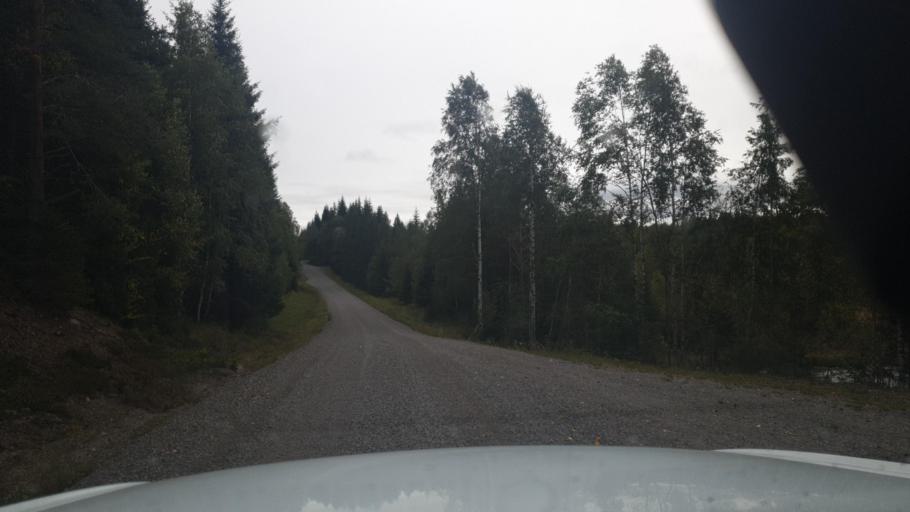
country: SE
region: Vaermland
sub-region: Eda Kommun
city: Charlottenberg
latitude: 60.1049
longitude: 12.6064
